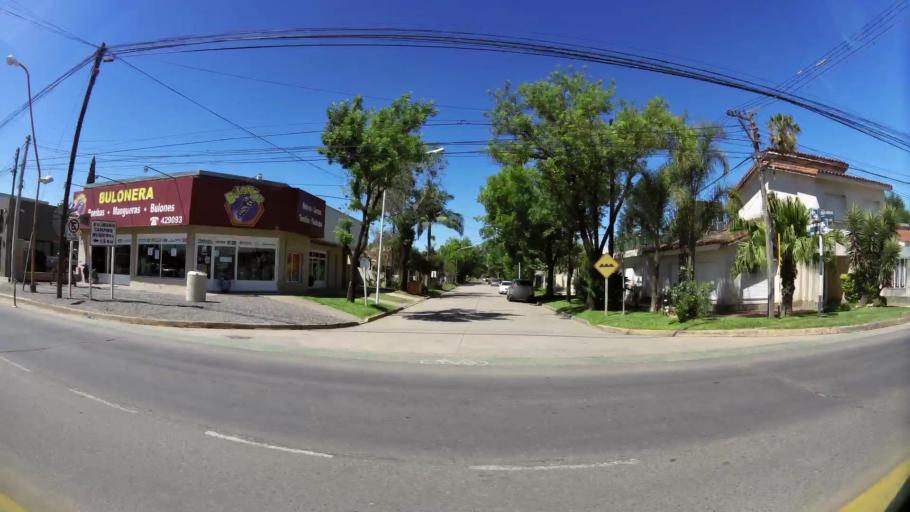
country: AR
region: Santa Fe
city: Esperanza
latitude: -31.4457
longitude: -60.9165
